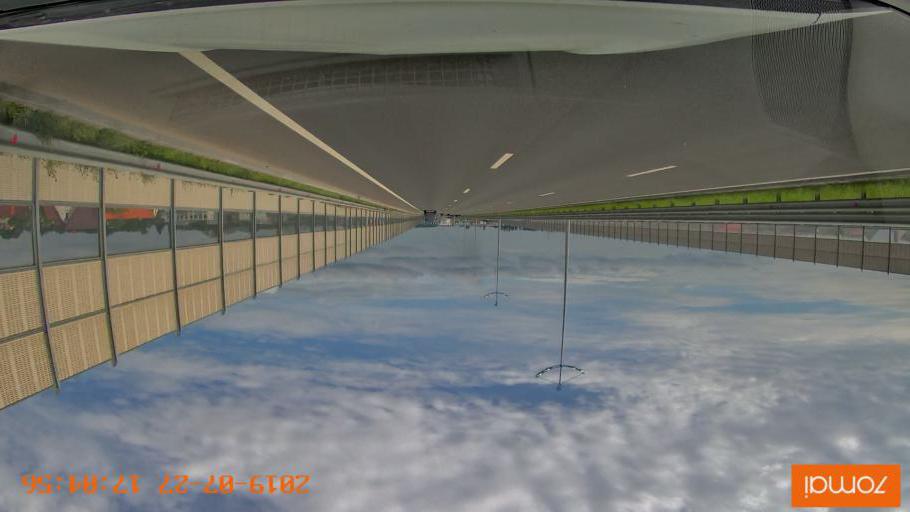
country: RU
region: Kaliningrad
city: Bol'shoe Isakovo
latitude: 54.7235
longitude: 20.5974
